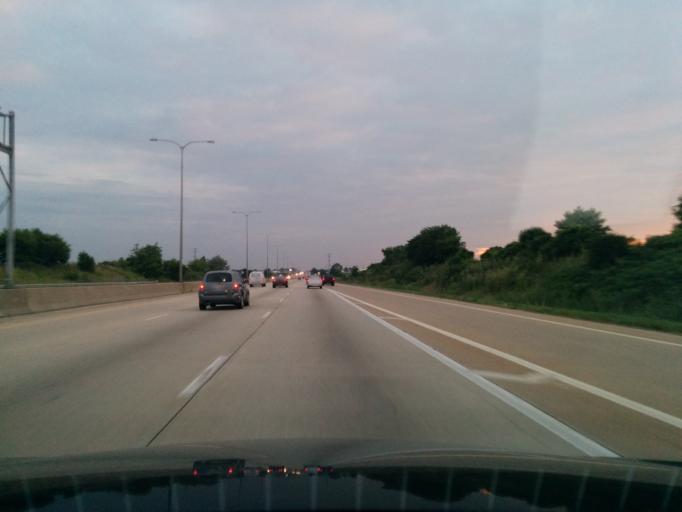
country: US
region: Illinois
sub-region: Cook County
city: Orland Hills
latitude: 41.5530
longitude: -87.8600
